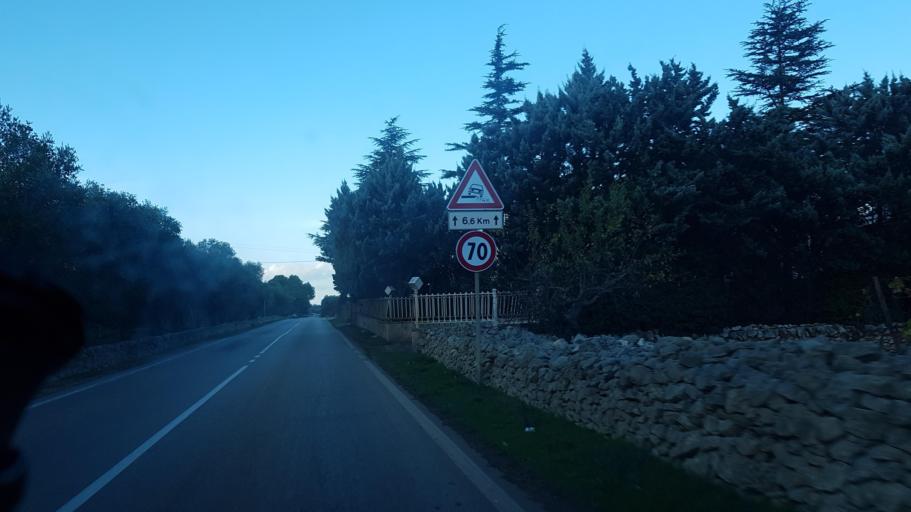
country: IT
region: Apulia
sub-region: Provincia di Brindisi
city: San Michele Salentino
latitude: 40.6632
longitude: 17.5999
